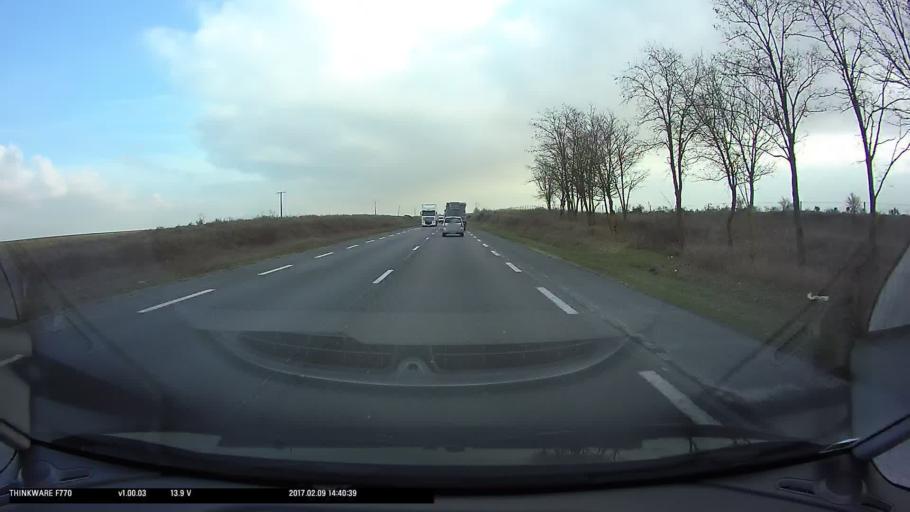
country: FR
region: Centre
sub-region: Departement du Cher
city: Trouy
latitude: 47.0388
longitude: 2.3583
